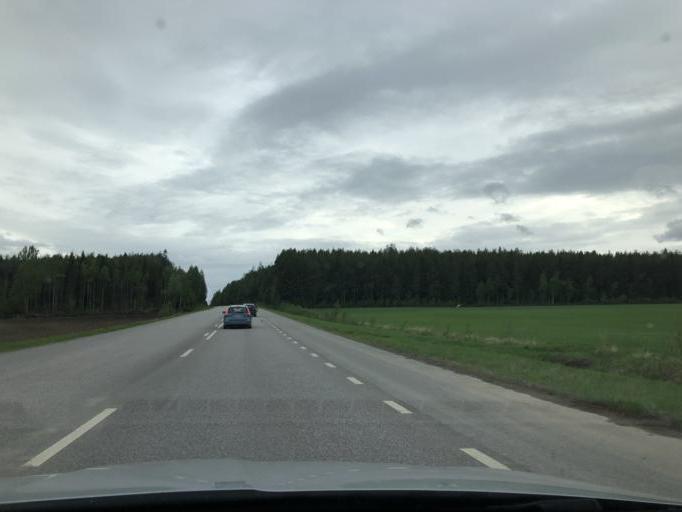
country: SE
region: Norrbotten
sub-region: Pitea Kommun
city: Norrfjarden
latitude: 65.3702
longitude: 21.4174
